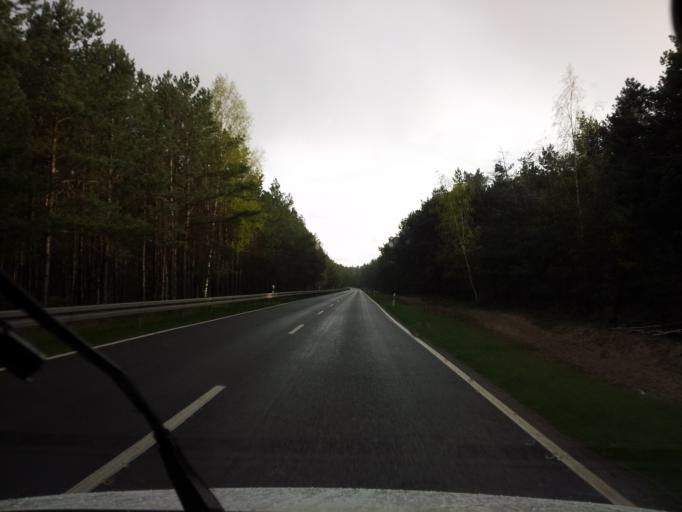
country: DE
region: Brandenburg
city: Heinersbruck
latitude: 51.7629
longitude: 14.4668
